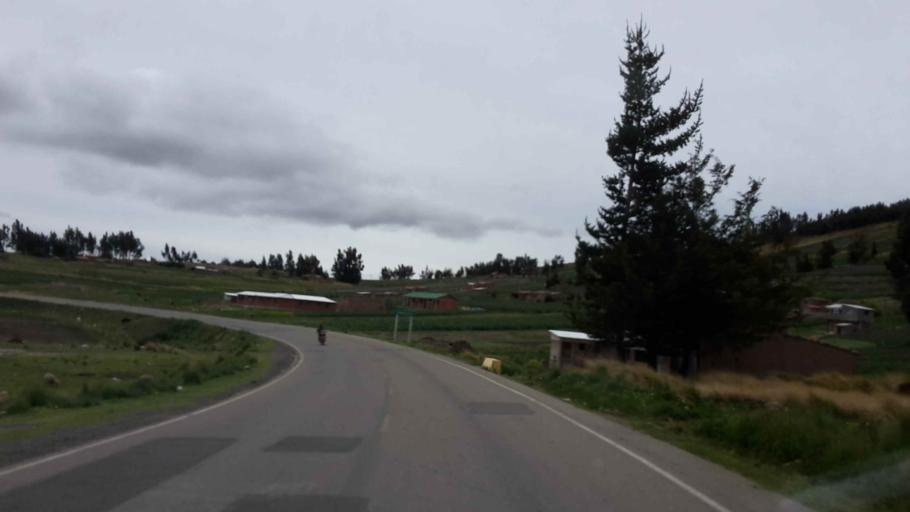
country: BO
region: Cochabamba
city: Arani
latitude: -17.4774
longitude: -65.6303
